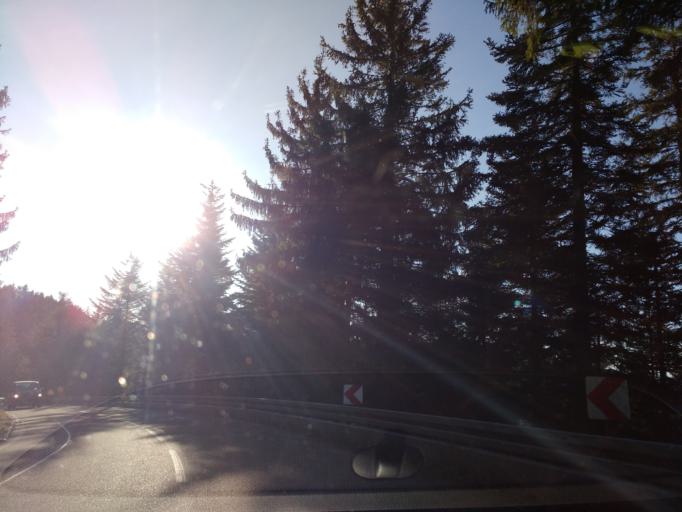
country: DE
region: Baden-Wuerttemberg
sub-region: Freiburg Region
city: Bad Peterstal-Griesbach
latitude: 48.4714
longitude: 8.2637
